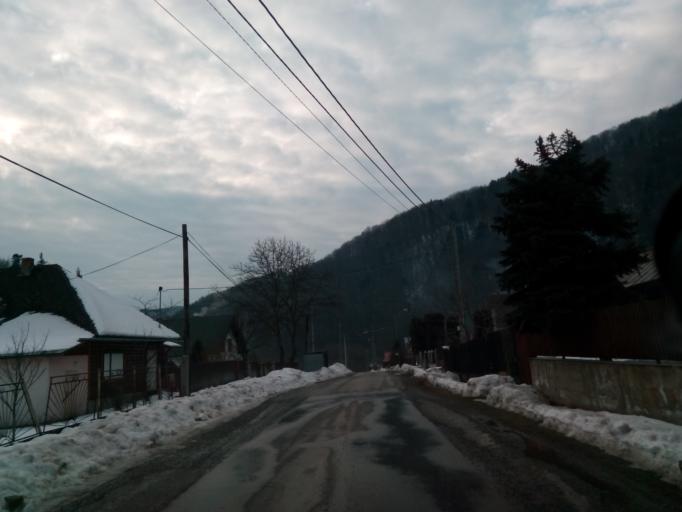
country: SK
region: Presovsky
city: Sabinov
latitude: 49.1918
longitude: 21.0856
